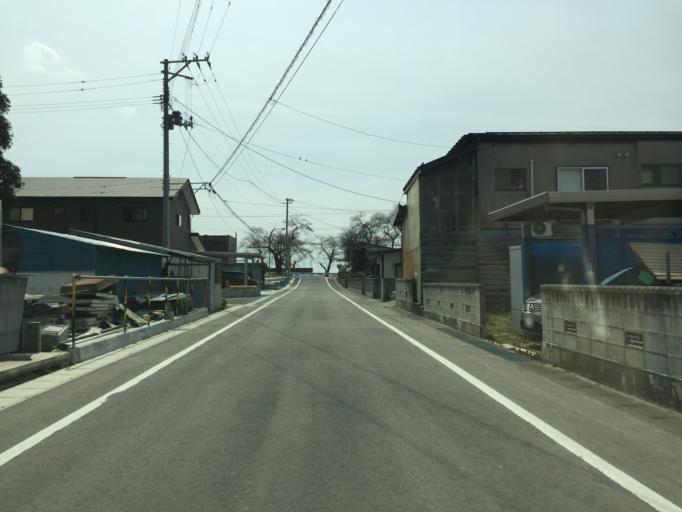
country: JP
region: Yamagata
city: Higashine
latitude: 38.4475
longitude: 140.3791
